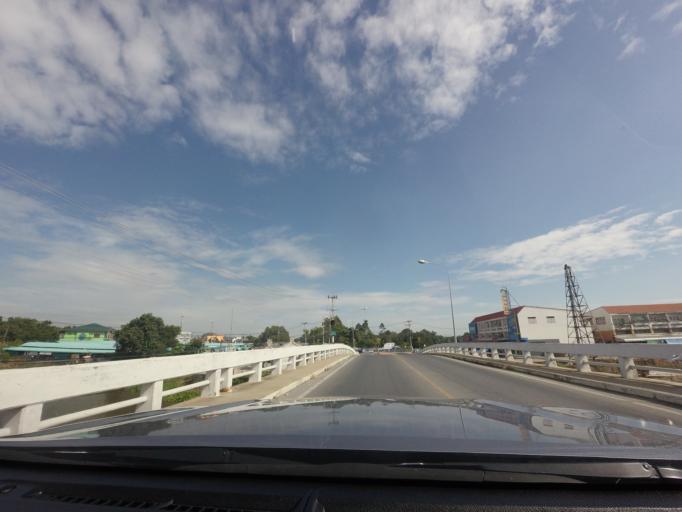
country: TH
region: Suphan Buri
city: Suphan Buri
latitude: 14.5370
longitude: 100.1232
